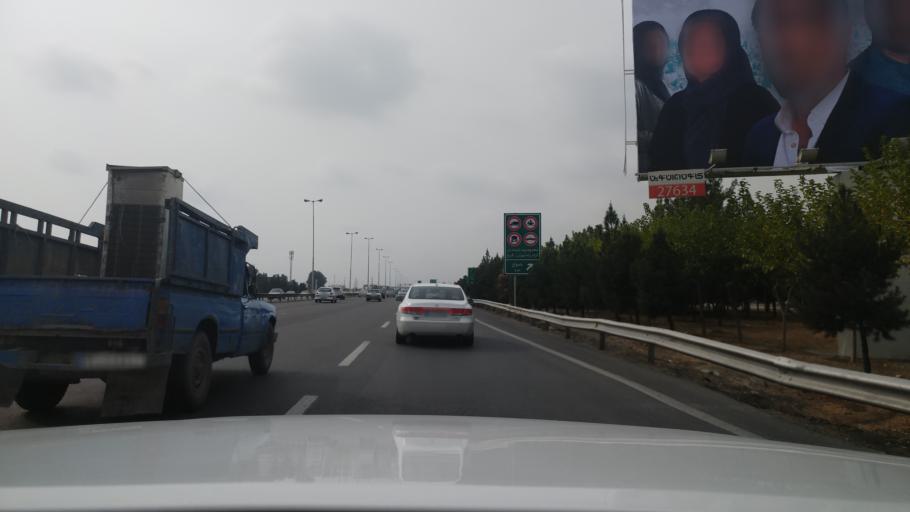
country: IR
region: Tehran
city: Shahr-e Qods
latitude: 35.7150
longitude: 51.2612
